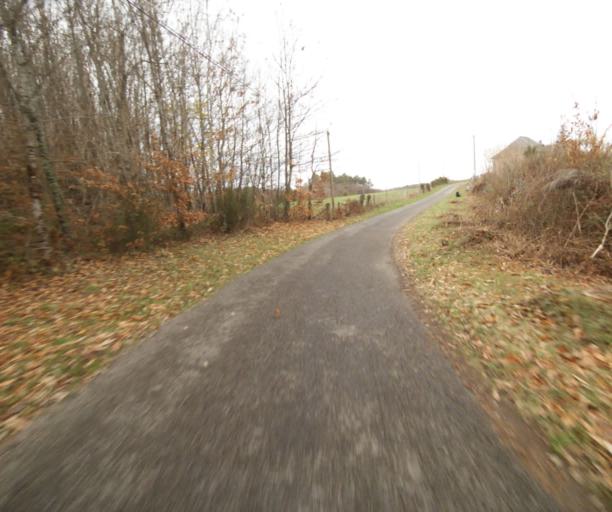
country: FR
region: Limousin
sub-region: Departement de la Correze
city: Chameyrat
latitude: 45.2332
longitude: 1.6837
